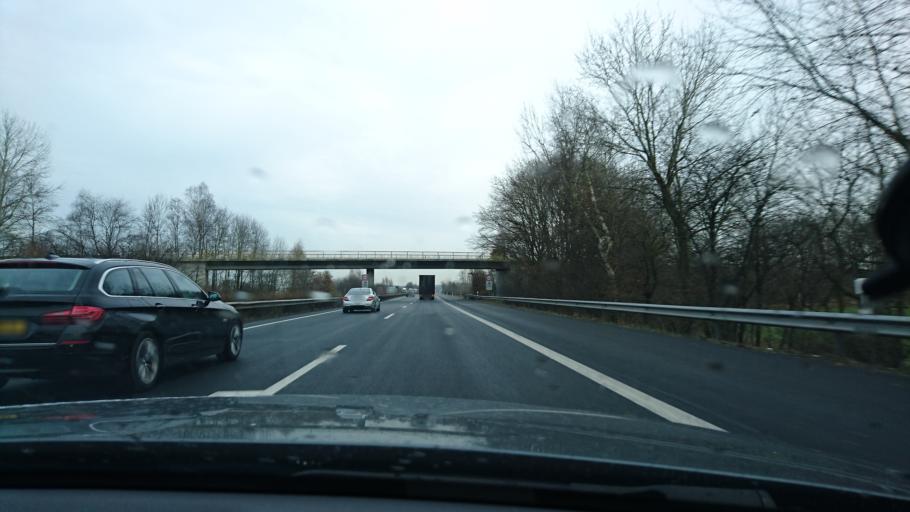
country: DE
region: Lower Saxony
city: Neuenkirchen
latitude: 52.4723
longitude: 8.0557
